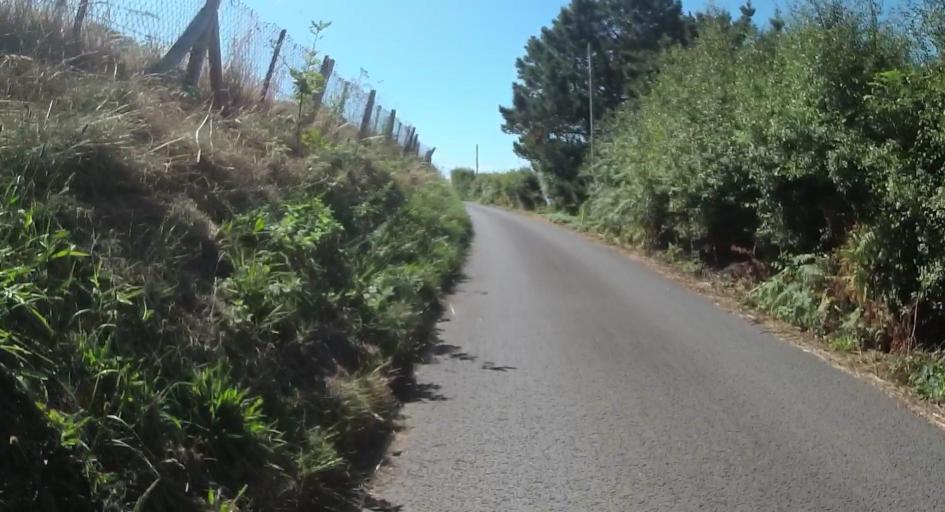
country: GB
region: England
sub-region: Isle of Wight
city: Chale
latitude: 50.6065
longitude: -1.3291
